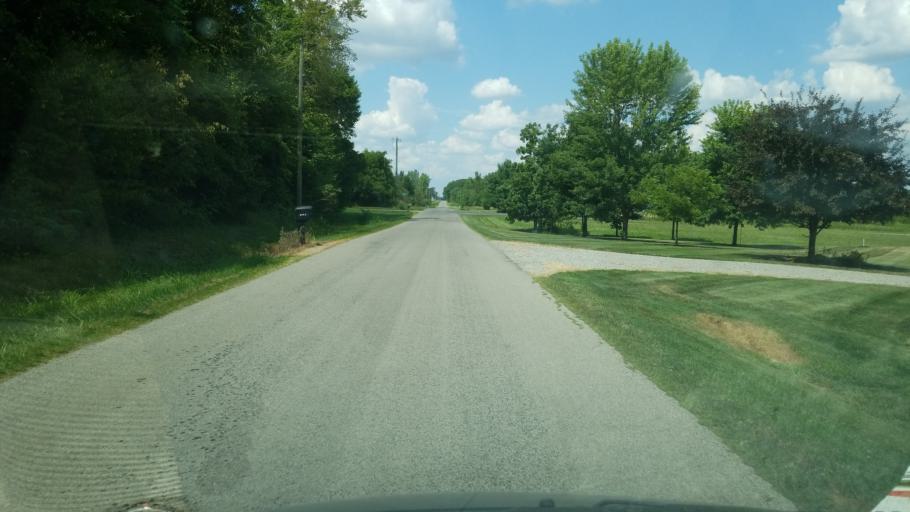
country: US
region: Ohio
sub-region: Champaign County
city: North Lewisburg
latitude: 40.3639
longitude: -83.4819
